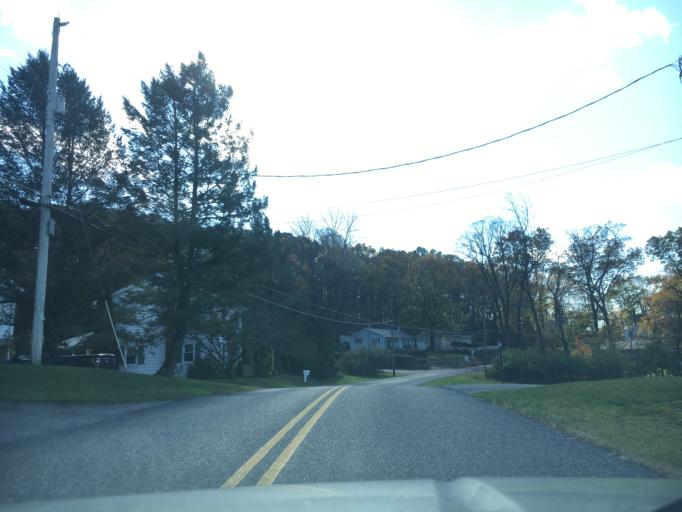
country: US
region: Pennsylvania
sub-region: Berks County
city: South Temple
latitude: 40.4029
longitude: -75.8880
